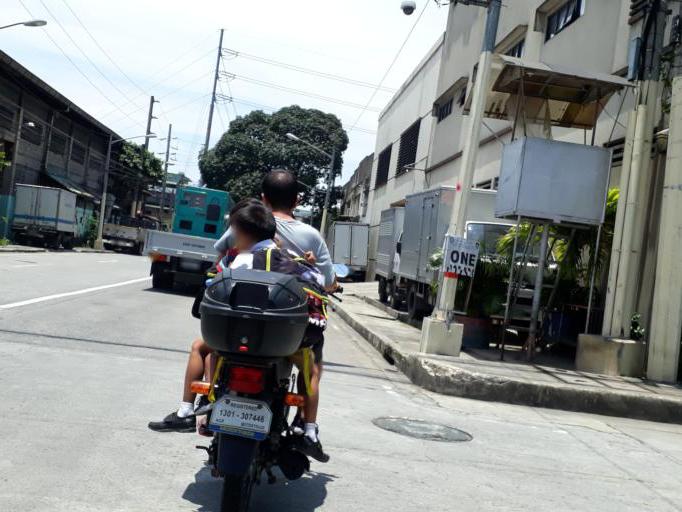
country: PH
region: Calabarzon
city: Del Monte
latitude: 14.6472
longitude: 120.9890
